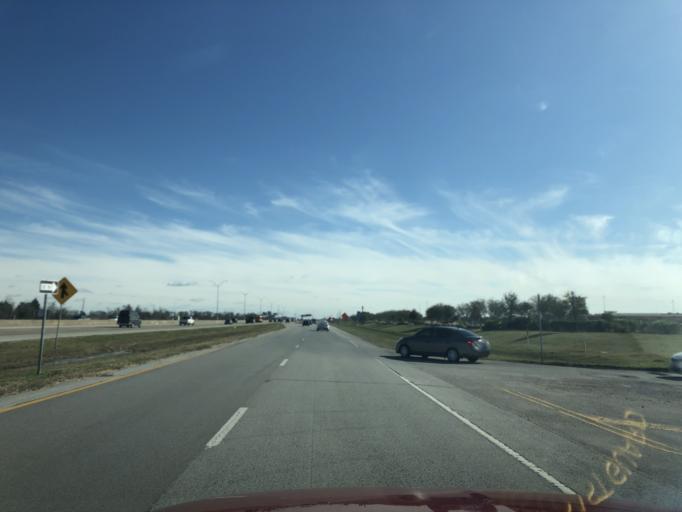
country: US
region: Texas
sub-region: Galveston County
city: Dickinson
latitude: 29.4281
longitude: -95.0586
